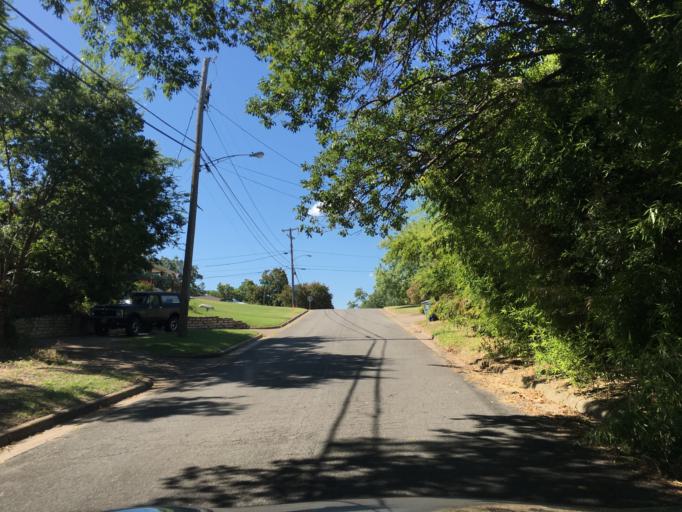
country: US
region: Texas
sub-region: Dallas County
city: Garland
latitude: 32.8707
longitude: -96.6973
